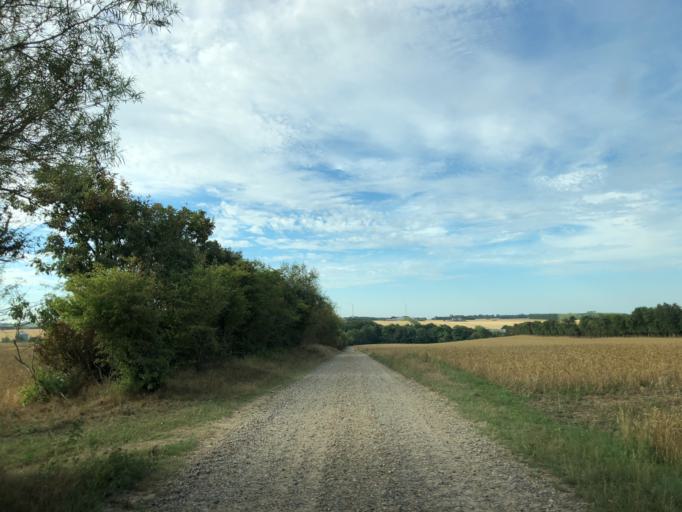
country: DK
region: Central Jutland
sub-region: Ringkobing-Skjern Kommune
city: Skjern
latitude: 56.0745
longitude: 8.4225
